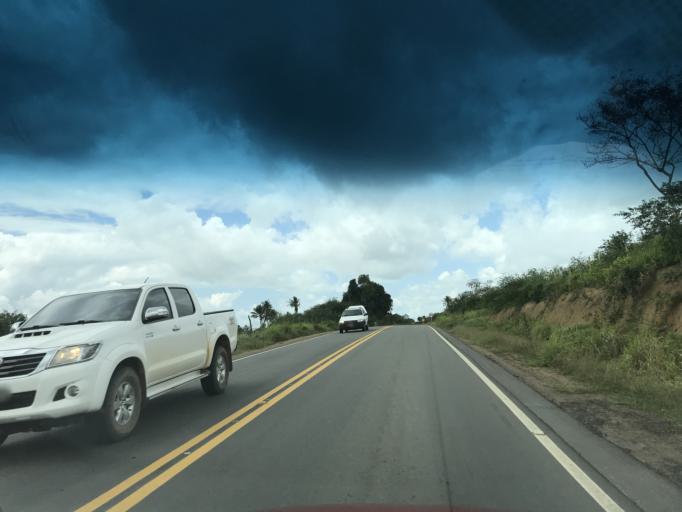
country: BR
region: Bahia
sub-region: Conceicao Do Almeida
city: Conceicao do Almeida
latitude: -12.7123
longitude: -39.2273
